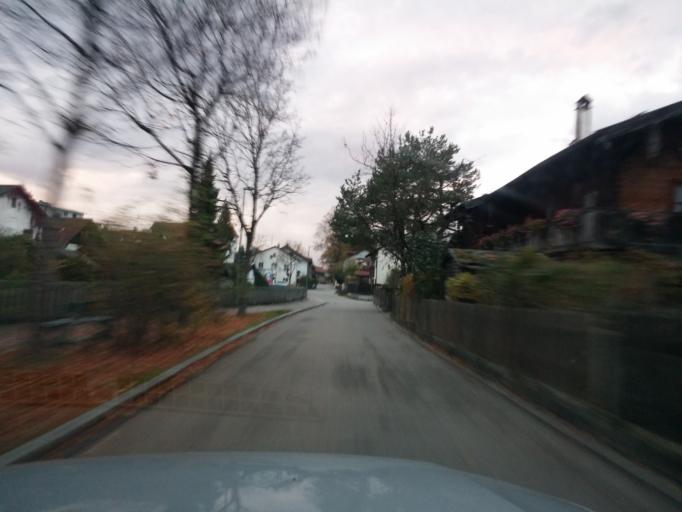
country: DE
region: Bavaria
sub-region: Upper Bavaria
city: Grafing bei Munchen
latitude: 48.0452
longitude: 11.9720
